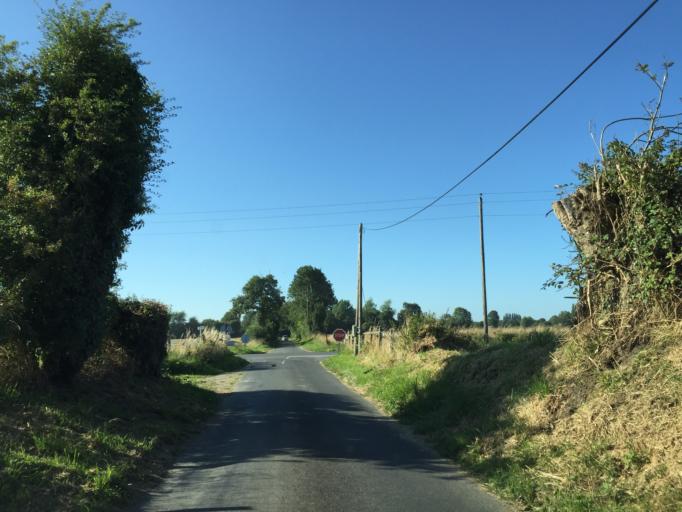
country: FR
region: Lower Normandy
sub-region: Departement du Calvados
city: Equemauville
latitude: 49.3969
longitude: 0.1990
